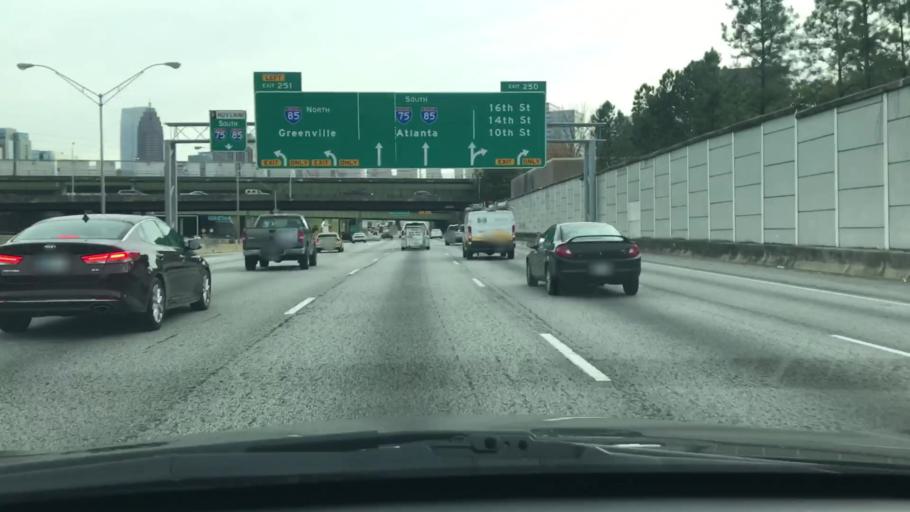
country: US
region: Georgia
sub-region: Fulton County
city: Atlanta
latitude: 33.7986
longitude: -84.3962
